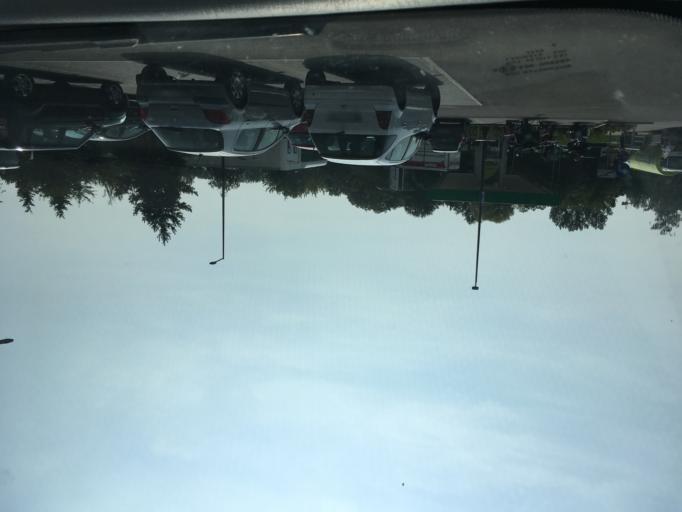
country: PL
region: Lesser Poland Voivodeship
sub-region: Powiat oswiecimski
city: Oswiecim
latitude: 50.0417
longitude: 19.2140
